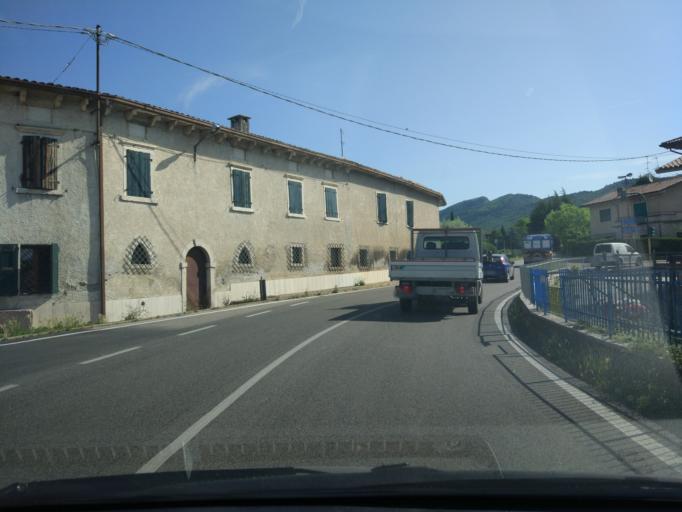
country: IT
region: Veneto
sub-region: Provincia di Verona
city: Rivoli Veronese
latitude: 45.5843
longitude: 10.8097
